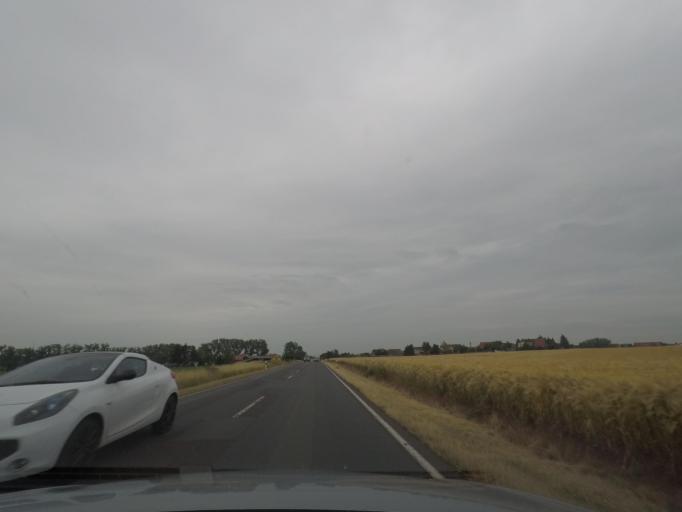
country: DE
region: Saxony-Anhalt
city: Oschersleben
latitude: 52.0448
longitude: 11.2631
